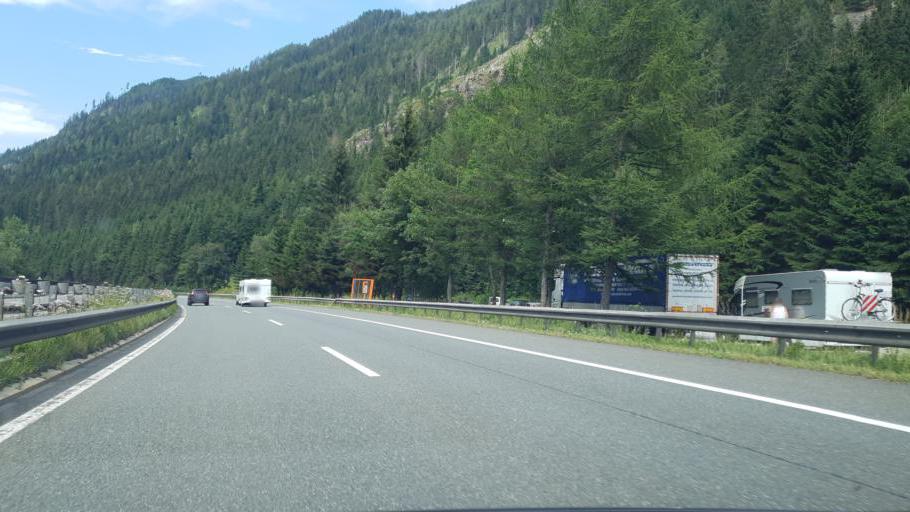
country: AT
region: Salzburg
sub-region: Politischer Bezirk Sankt Johann im Pongau
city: Flachau
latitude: 47.3121
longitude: 13.3961
